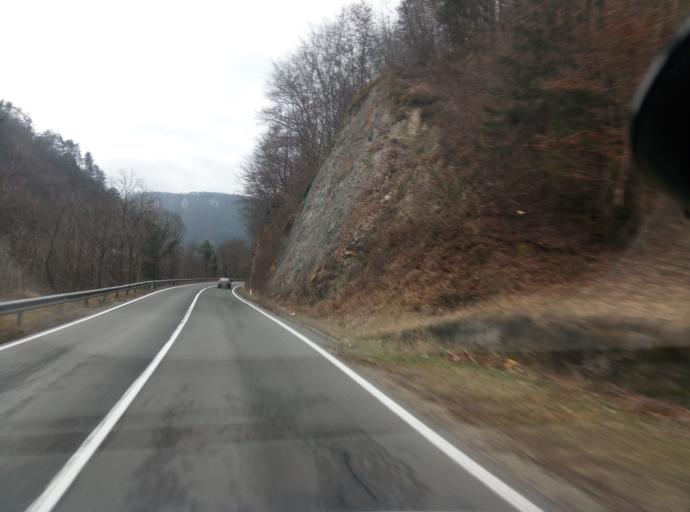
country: SI
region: Zagorje ob Savi
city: Kisovec
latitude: 46.0920
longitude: 14.9297
